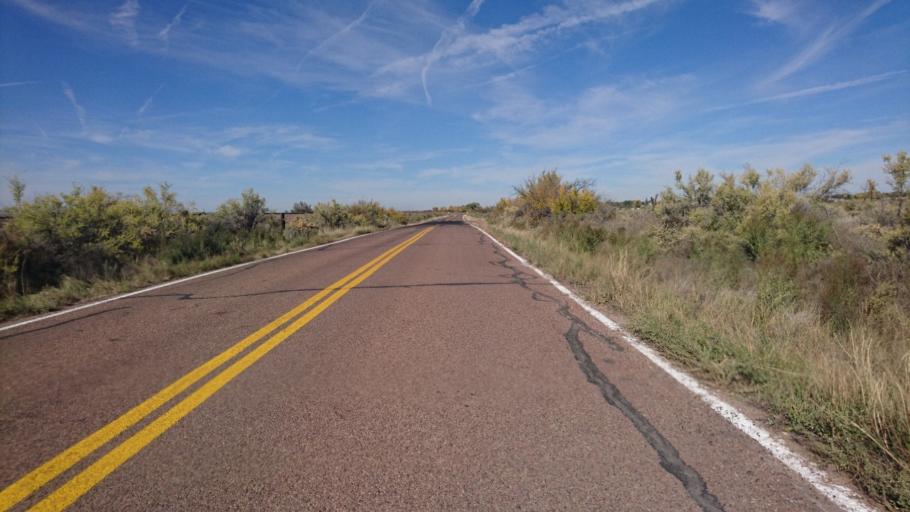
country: US
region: Arizona
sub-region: Navajo County
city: Joseph City
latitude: 34.9458
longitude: -110.3261
